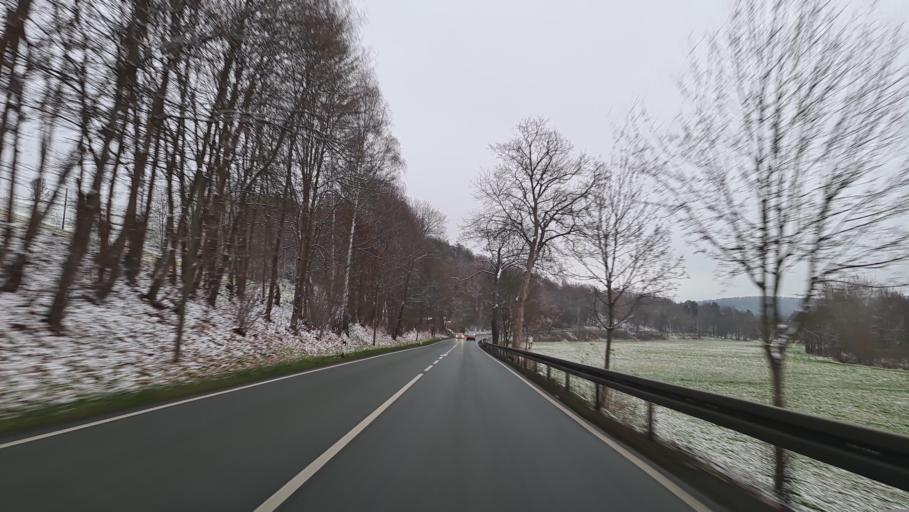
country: DE
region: Saxony
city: Adorf
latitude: 50.3152
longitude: 12.2841
